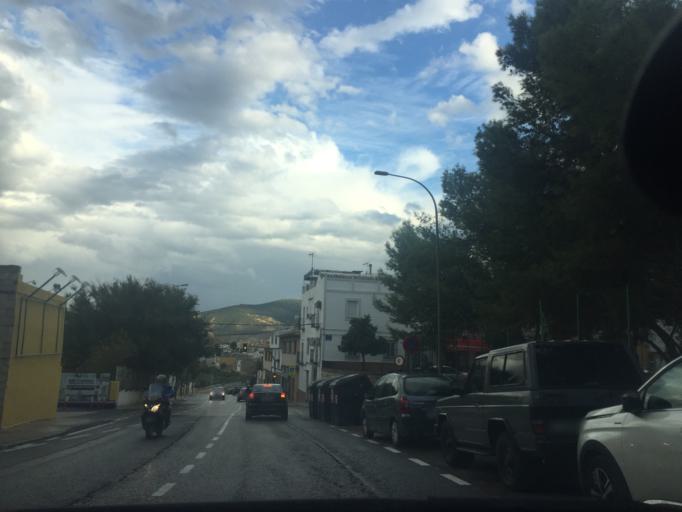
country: ES
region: Andalusia
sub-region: Provincia de Jaen
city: Jaen
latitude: 37.7680
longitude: -3.7772
